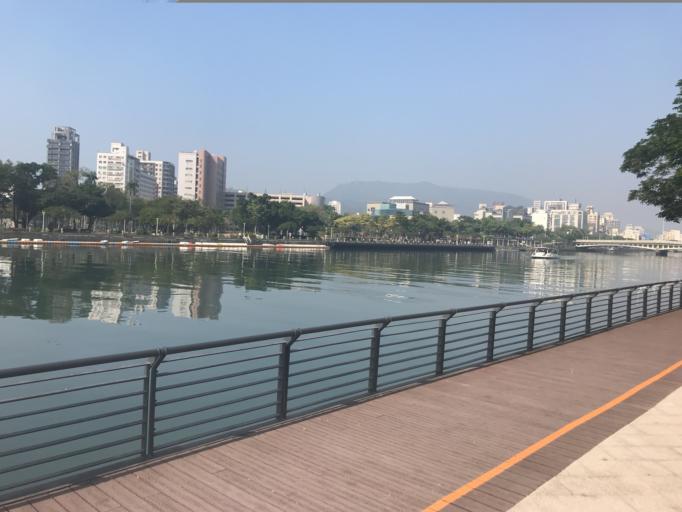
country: TW
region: Kaohsiung
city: Kaohsiung
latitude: 22.6238
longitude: 120.2902
